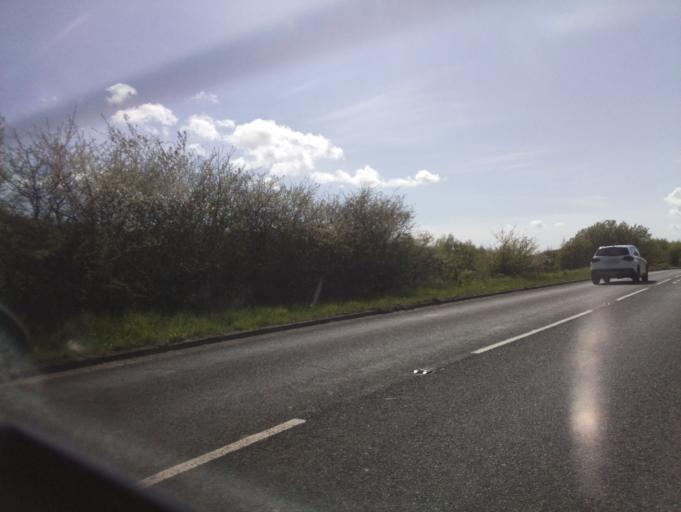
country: GB
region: Wales
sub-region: Caerphilly County Borough
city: Caerphilly
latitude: 51.5591
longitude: -3.2209
